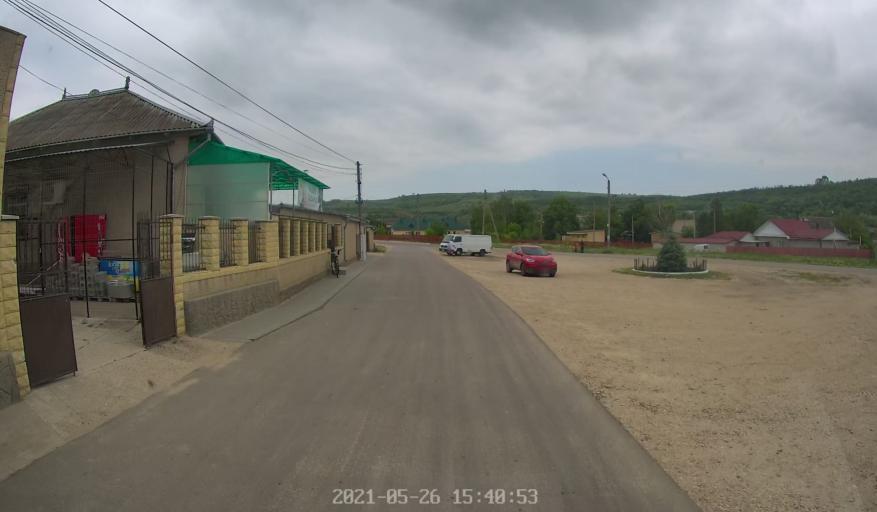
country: MD
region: Hincesti
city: Dancu
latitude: 46.6665
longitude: 28.3260
